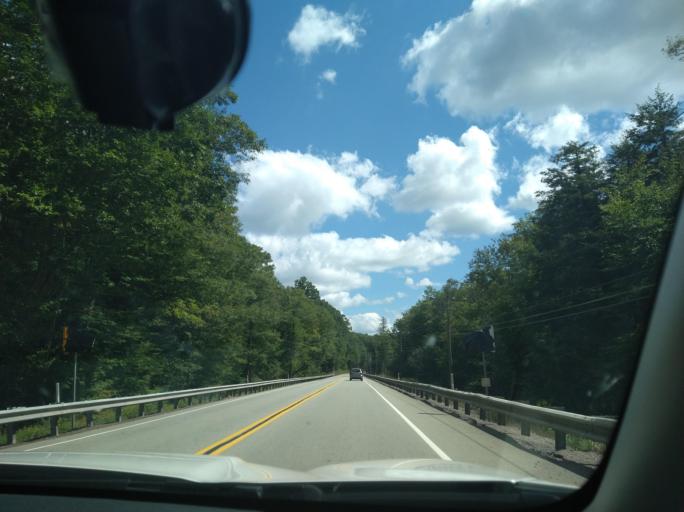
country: US
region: Pennsylvania
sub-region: Somerset County
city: Somerset
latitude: 40.0629
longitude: -79.2320
